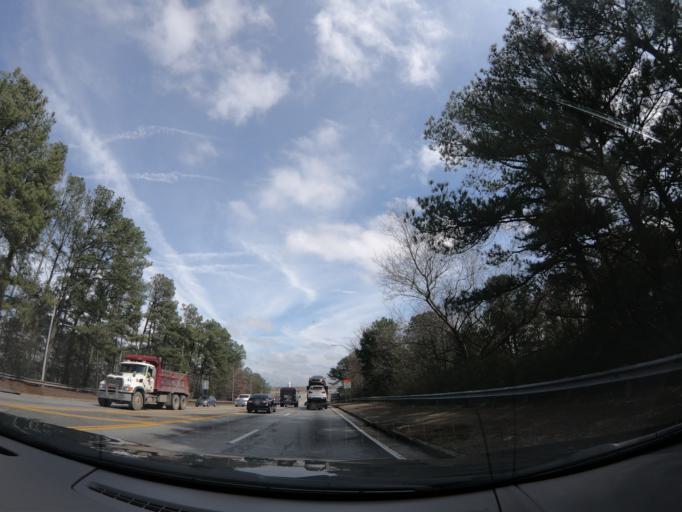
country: US
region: Georgia
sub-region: Fulton County
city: College Park
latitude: 33.6296
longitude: -84.4542
